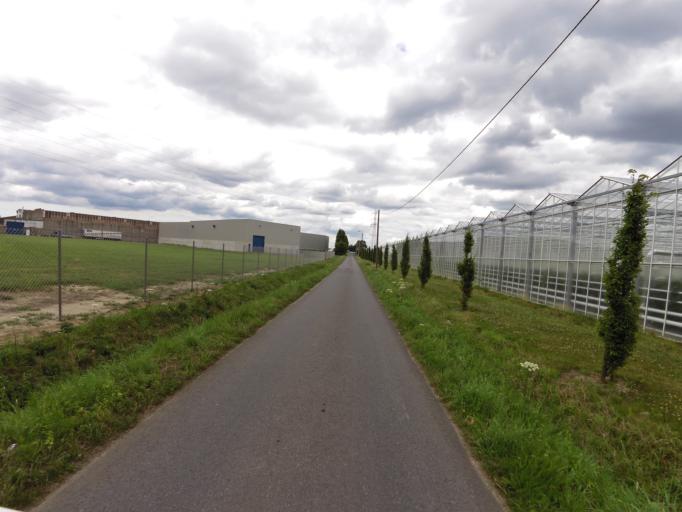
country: BE
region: Flanders
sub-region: Provincie West-Vlaanderen
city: Hooglede
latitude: 50.9572
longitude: 3.0600
